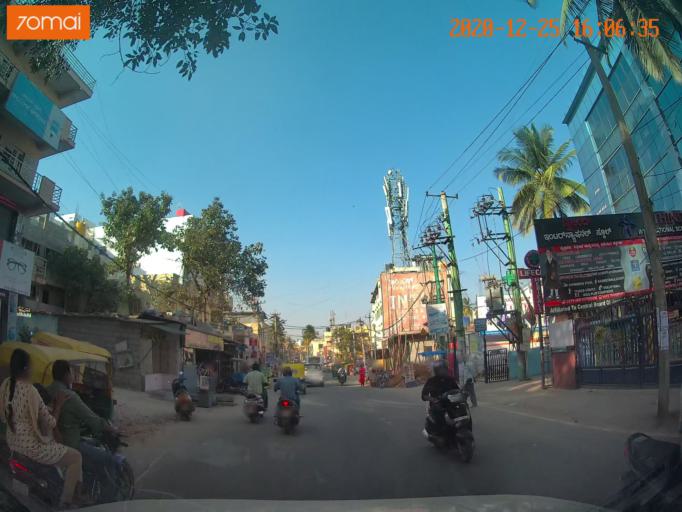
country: IN
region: Karnataka
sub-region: Bangalore Urban
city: Bangalore
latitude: 12.8923
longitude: 77.6259
